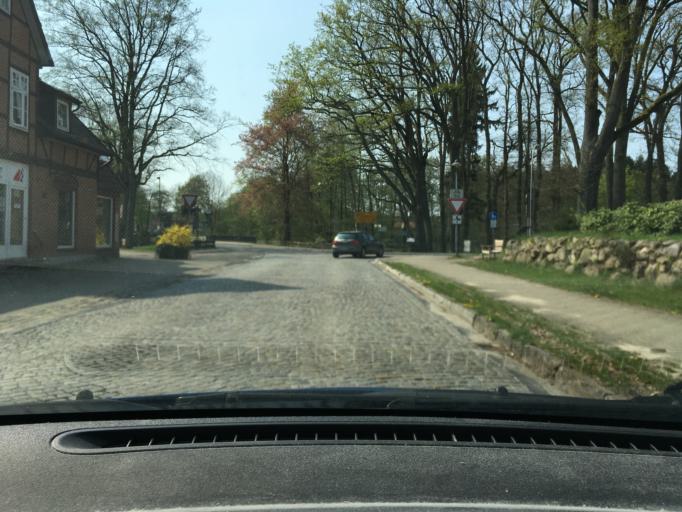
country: DE
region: Lower Saxony
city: Hermannsburg
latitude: 52.8772
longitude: 10.1139
